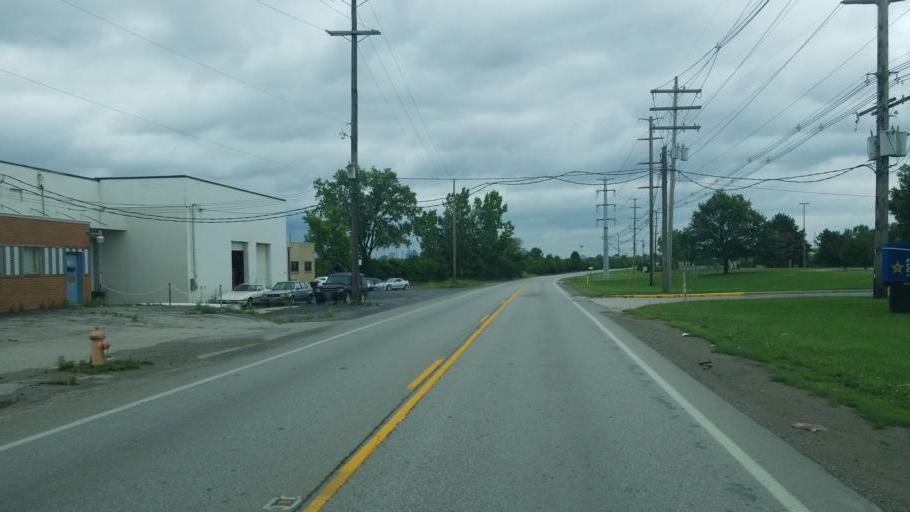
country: US
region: Ohio
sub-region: Franklin County
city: Columbus
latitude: 39.9076
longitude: -83.0221
